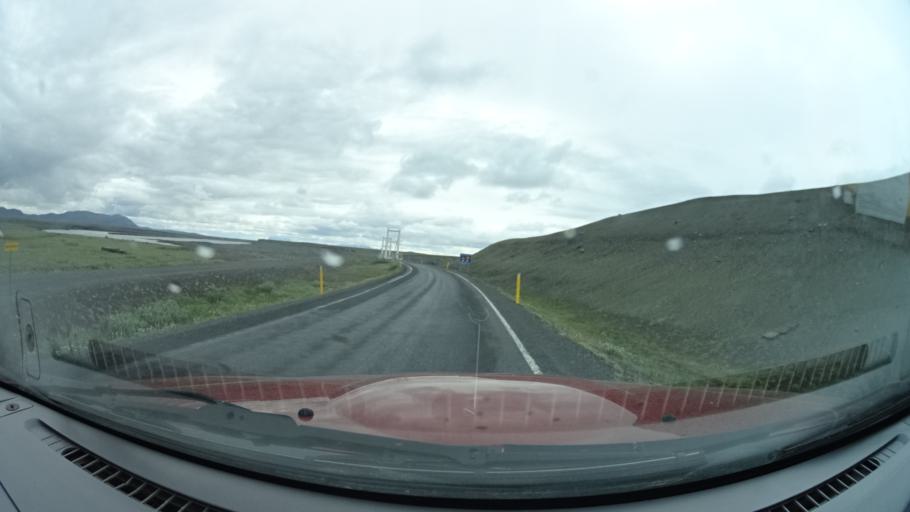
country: IS
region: Northeast
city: Laugar
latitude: 65.6250
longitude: -16.1883
